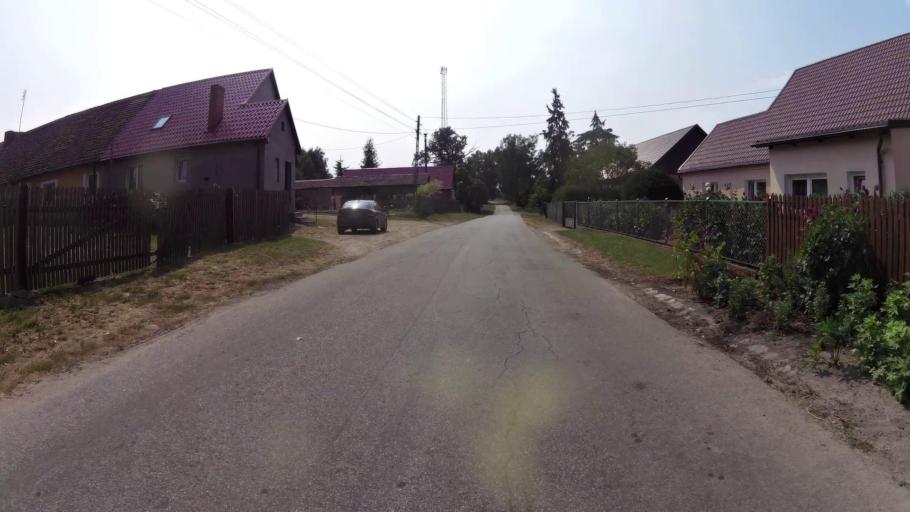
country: PL
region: West Pomeranian Voivodeship
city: Trzcinsko Zdroj
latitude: 52.9174
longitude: 14.5366
